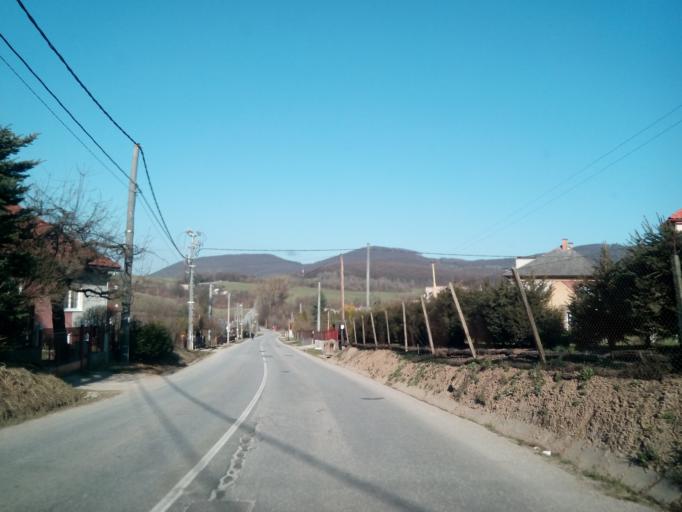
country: SK
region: Kosicky
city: Roznava
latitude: 48.6656
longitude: 20.4377
